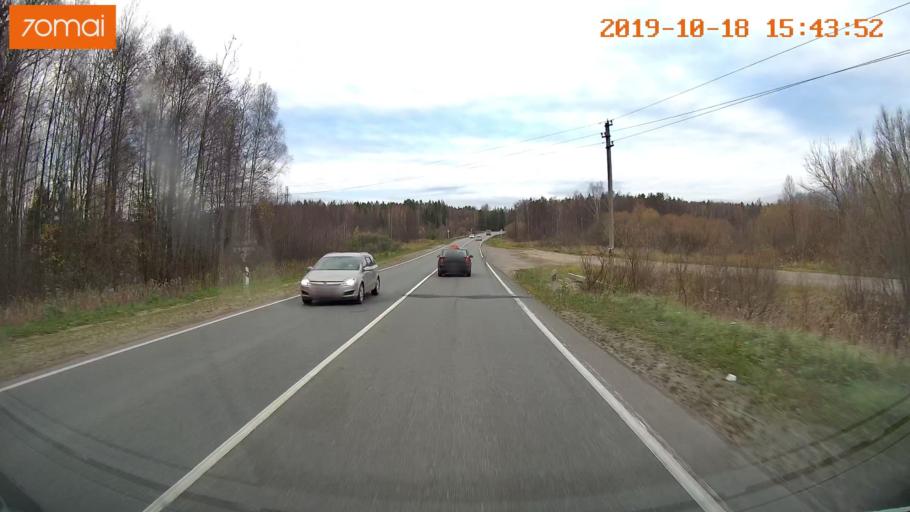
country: RU
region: Vladimir
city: Golovino
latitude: 55.9738
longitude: 40.5474
